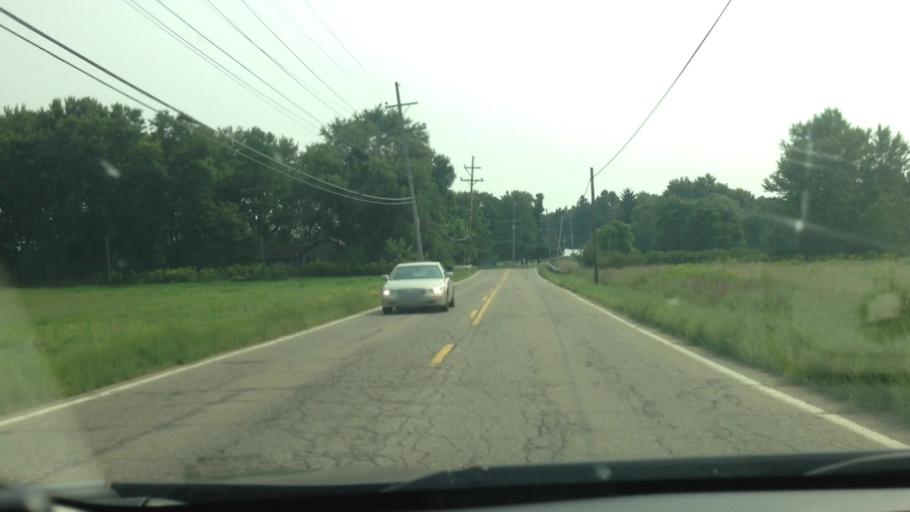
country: US
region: Ohio
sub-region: Summit County
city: Fairlawn
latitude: 41.0932
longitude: -81.5900
